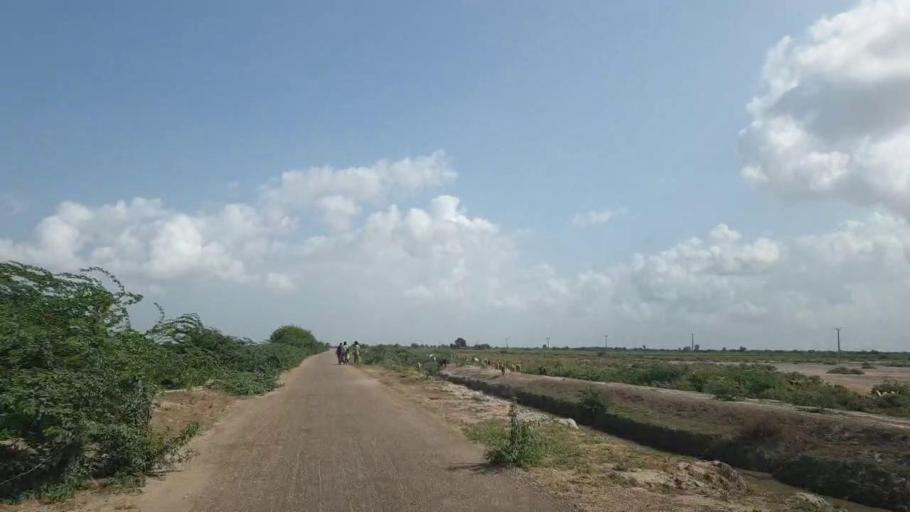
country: PK
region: Sindh
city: Kadhan
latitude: 24.5725
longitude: 69.0672
